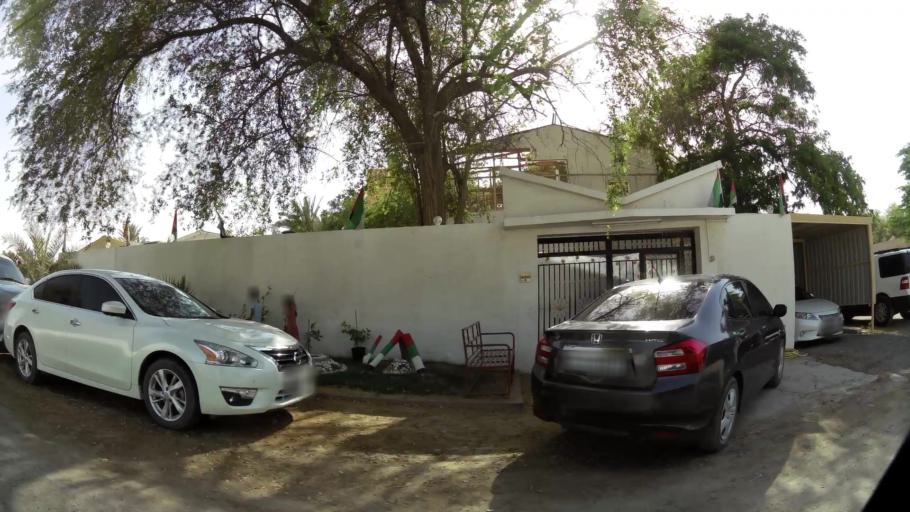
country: AE
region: Dubai
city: Dubai
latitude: 25.1615
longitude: 55.2721
